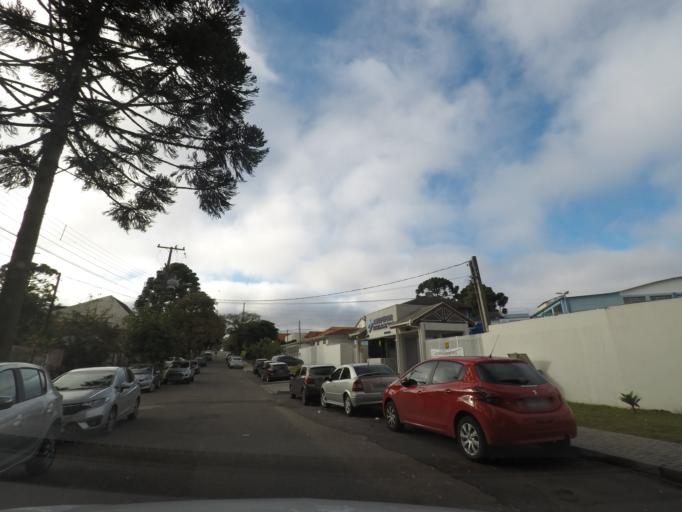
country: BR
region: Parana
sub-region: Pinhais
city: Pinhais
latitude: -25.4554
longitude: -49.2357
